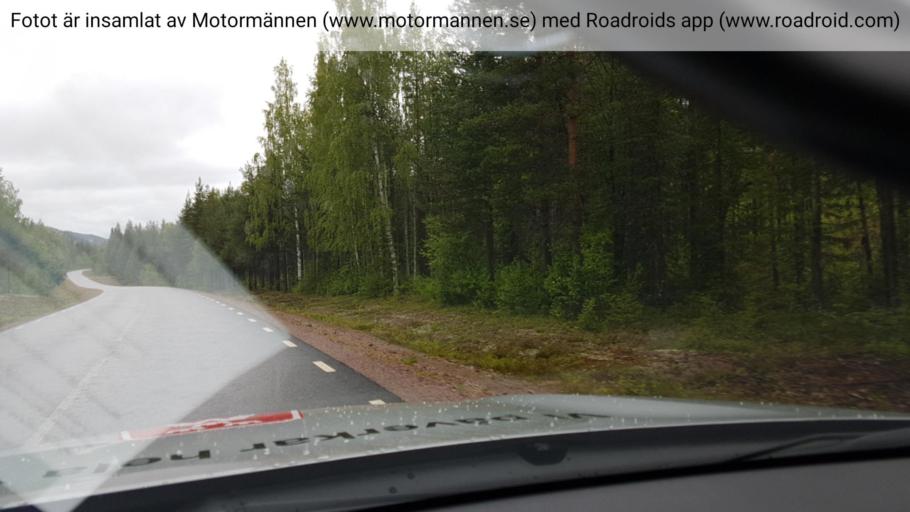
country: SE
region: Norrbotten
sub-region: Gallivare Kommun
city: Gaellivare
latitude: 66.6509
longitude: 20.3861
